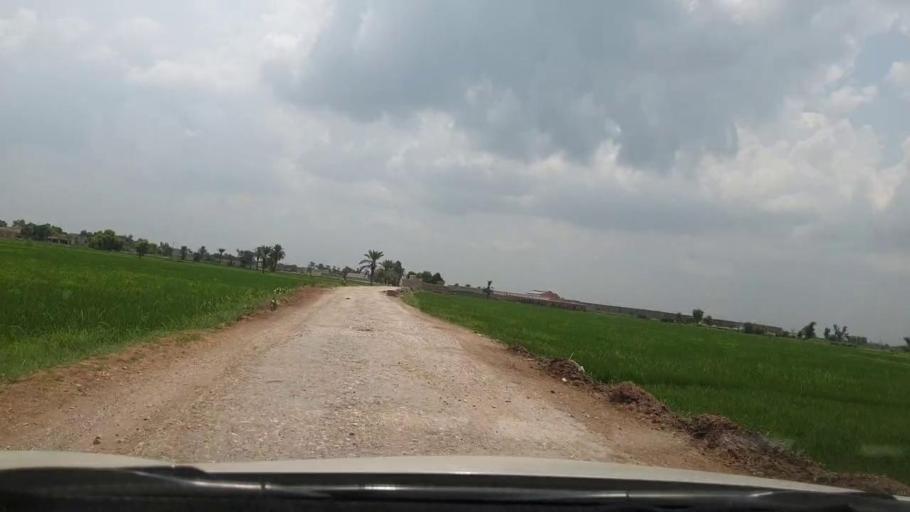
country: PK
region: Sindh
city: Goth Garelo
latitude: 27.4245
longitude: 68.1101
